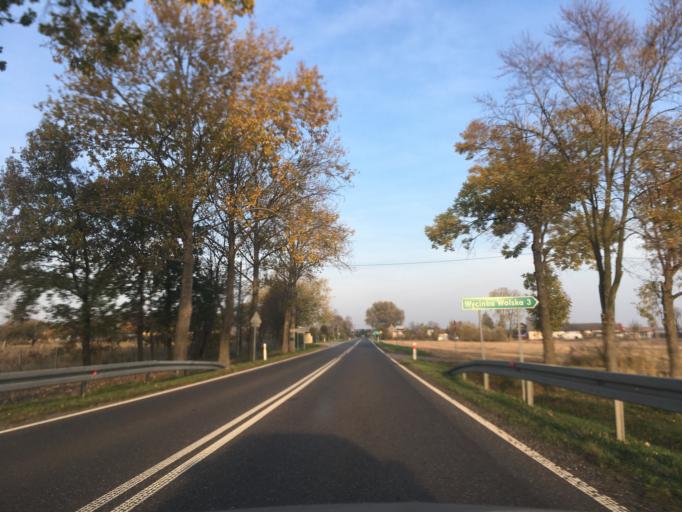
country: PL
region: Lodz Voivodeship
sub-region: Powiat skierniewicki
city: Kowiesy
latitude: 51.9223
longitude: 20.4135
